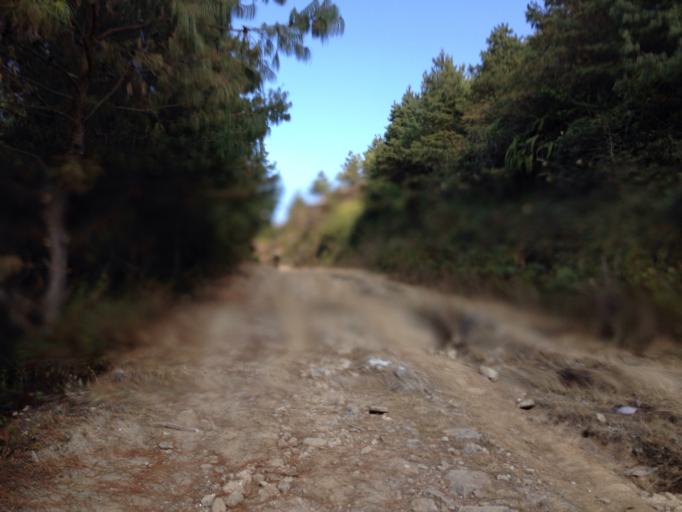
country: NP
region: Central Region
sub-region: Bagmati Zone
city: Nagarkot
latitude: 27.8227
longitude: 85.4467
